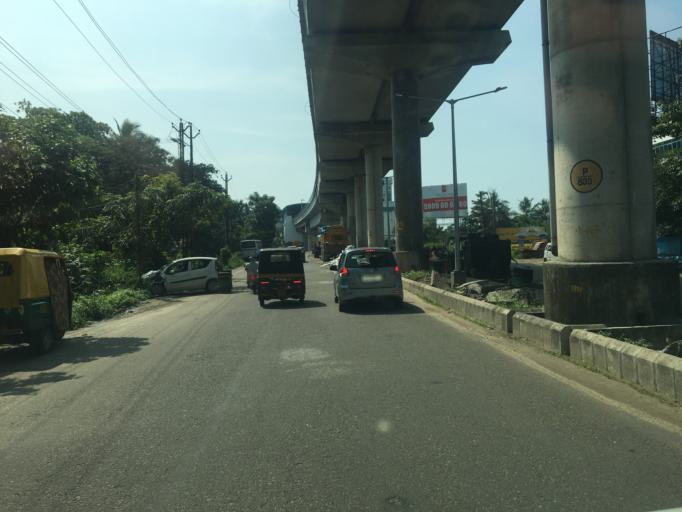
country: IN
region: Kerala
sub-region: Ernakulam
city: Cochin
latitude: 9.9675
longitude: 76.3108
